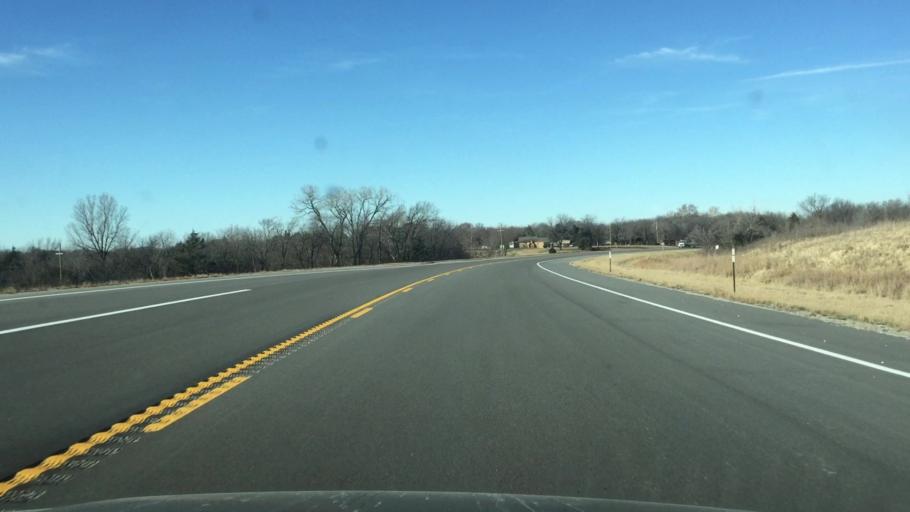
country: US
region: Kansas
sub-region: Franklin County
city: Ottawa
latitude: 38.4716
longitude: -95.2654
